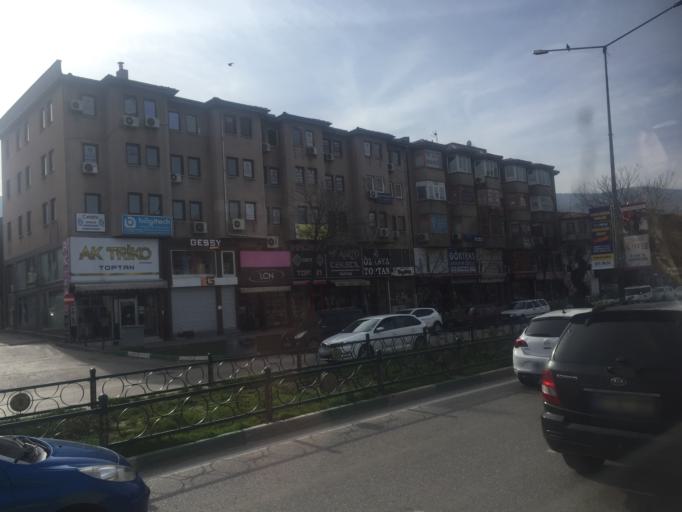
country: TR
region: Bursa
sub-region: Osmangazi
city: Bursa
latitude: 40.1879
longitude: 29.0662
